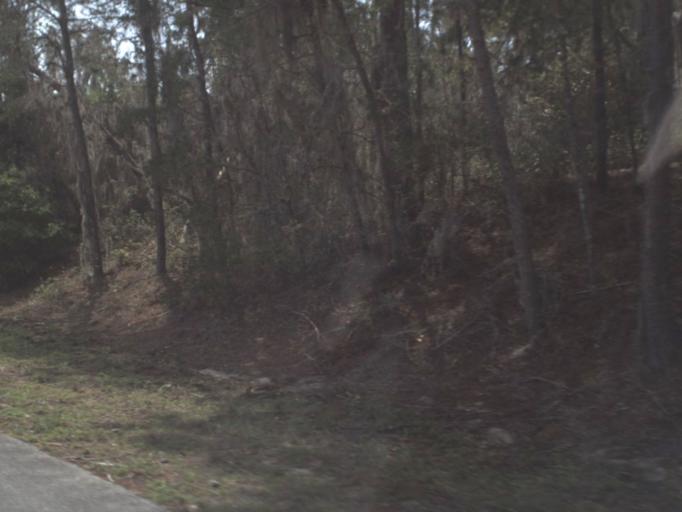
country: US
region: Florida
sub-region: Lake County
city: Astor
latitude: 29.3005
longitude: -81.6706
